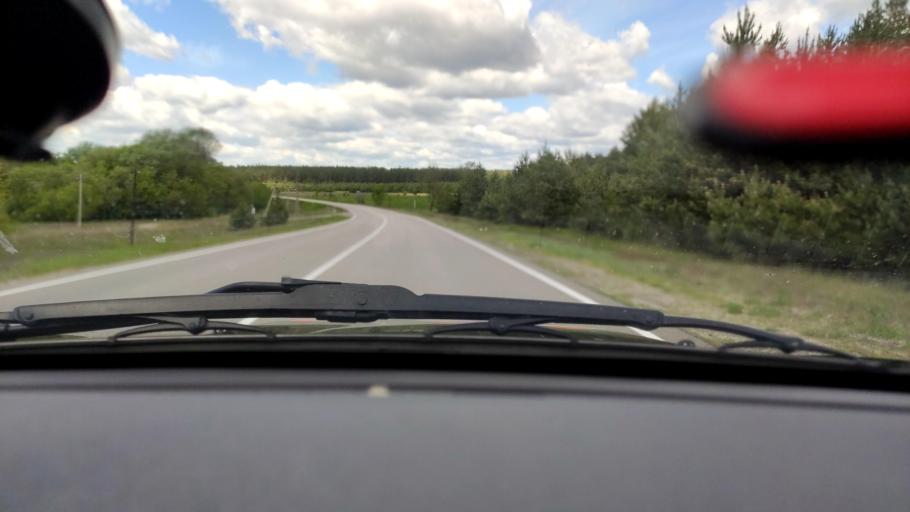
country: RU
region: Voronezj
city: Uryv-Pokrovka
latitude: 51.0543
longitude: 38.9588
